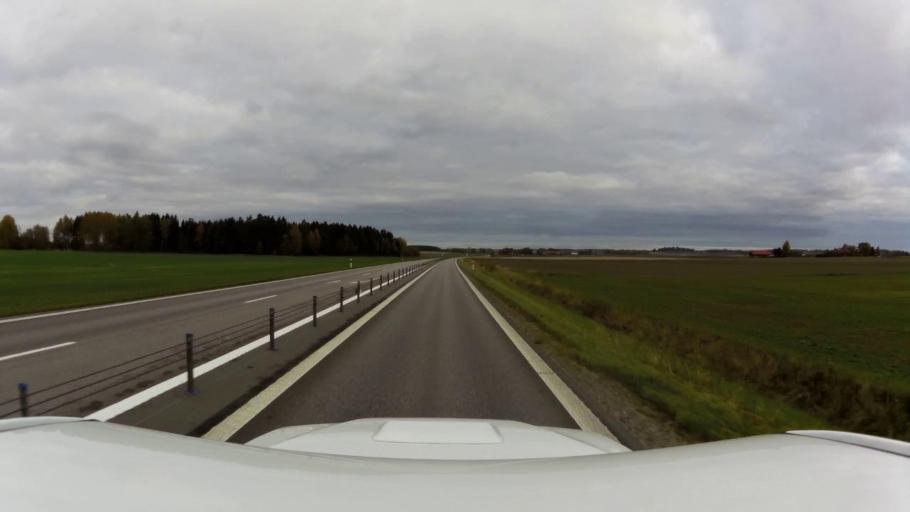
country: SE
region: OEstergoetland
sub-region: Linkopings Kommun
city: Berg
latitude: 58.4561
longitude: 15.5012
